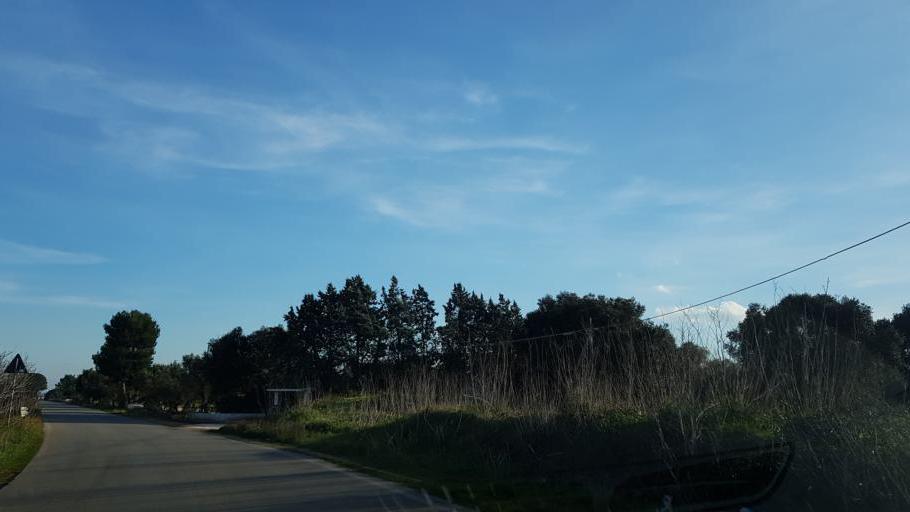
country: IT
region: Apulia
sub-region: Provincia di Brindisi
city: San Vito dei Normanni
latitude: 40.6850
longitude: 17.7662
